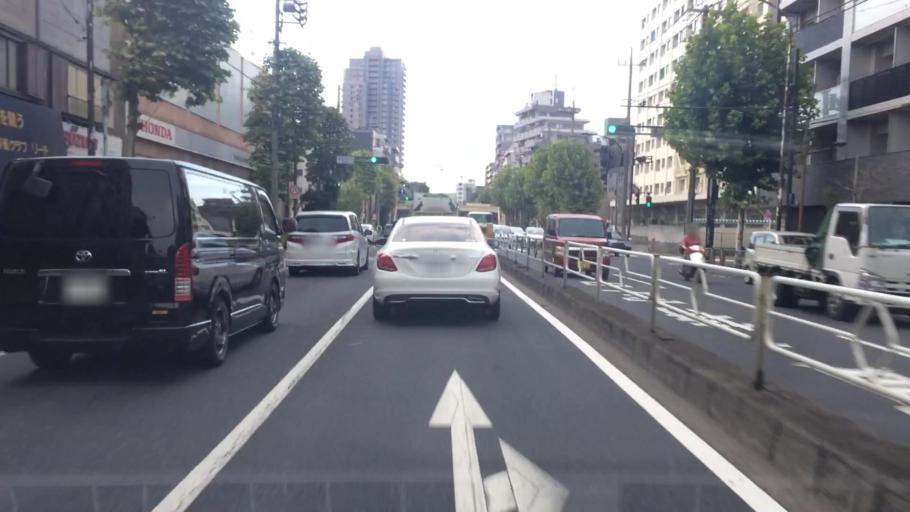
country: JP
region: Tokyo
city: Tokyo
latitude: 35.6932
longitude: 139.6544
